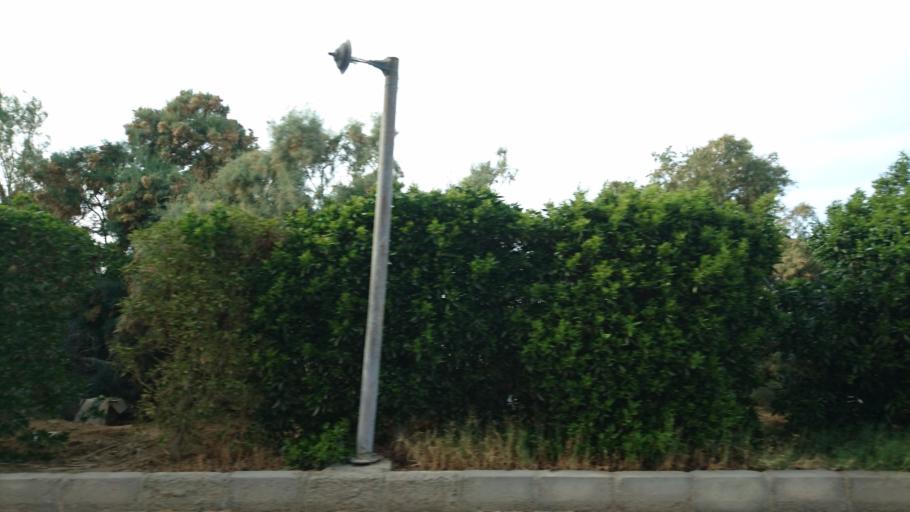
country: EG
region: Red Sea
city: Bur Safajah
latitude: 26.8013
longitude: 33.9404
